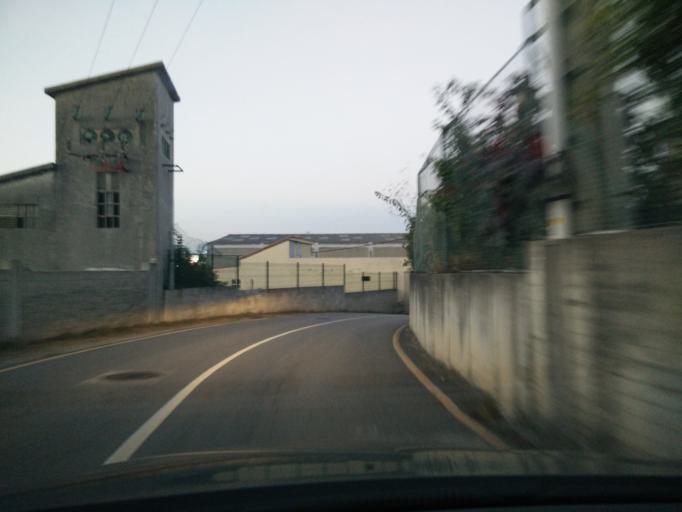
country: ES
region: Galicia
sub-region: Provincia da Coruna
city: A Coruna
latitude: 43.3460
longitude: -8.4252
